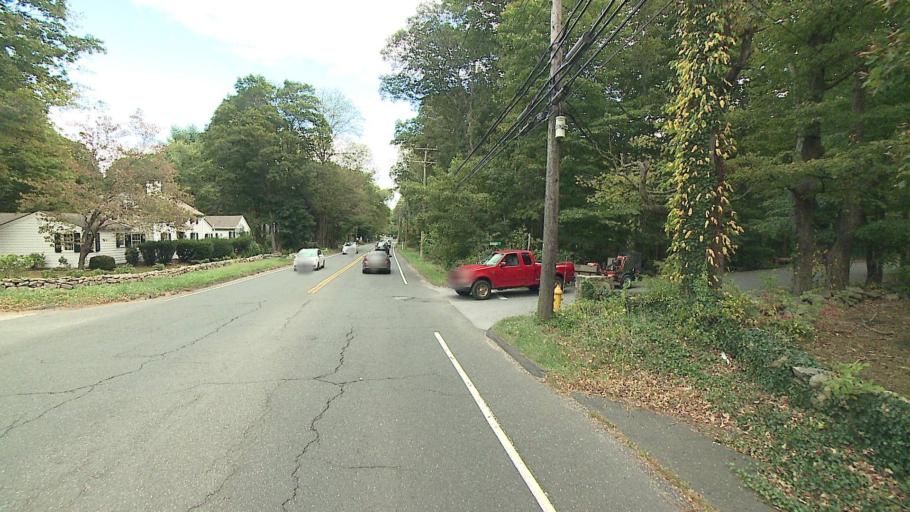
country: US
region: Connecticut
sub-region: Fairfield County
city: Wilton
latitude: 41.1802
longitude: -73.4123
